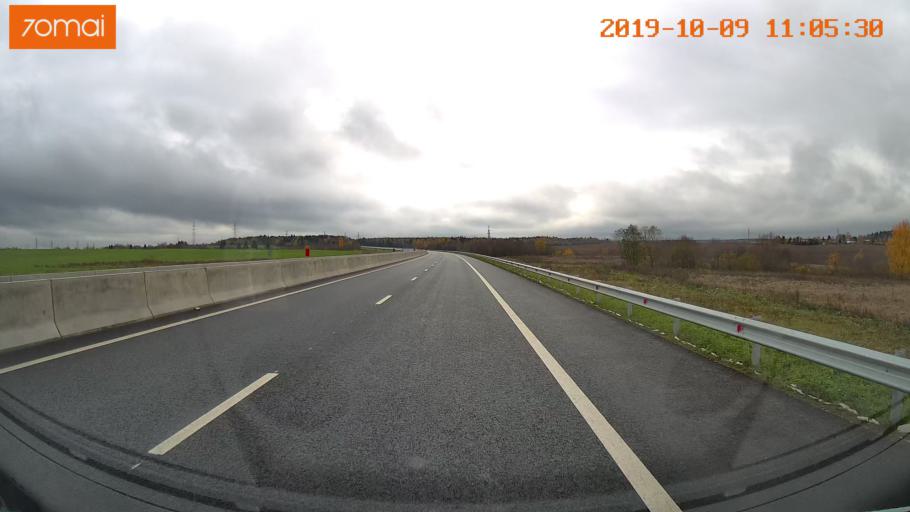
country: RU
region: Vologda
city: Molochnoye
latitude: 59.1993
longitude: 39.7582
